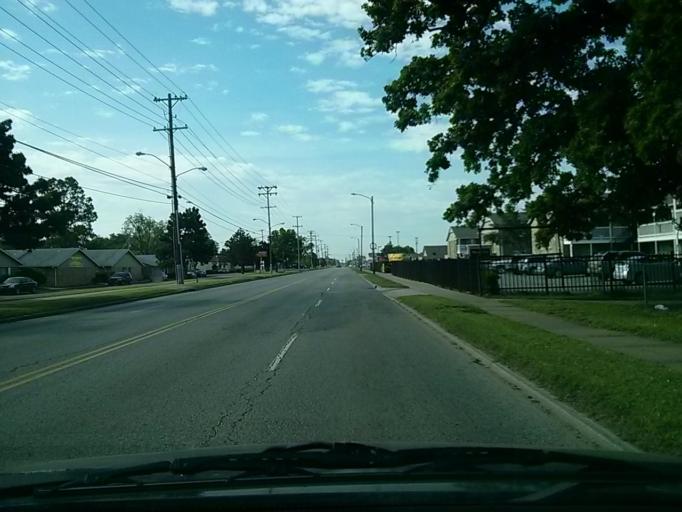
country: US
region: Oklahoma
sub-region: Tulsa County
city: Jenks
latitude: 36.0810
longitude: -95.9759
